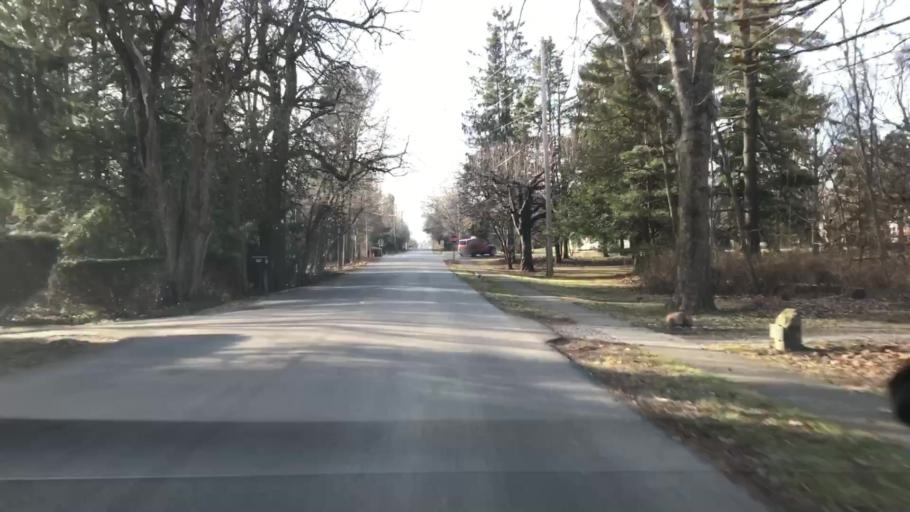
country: US
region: Ohio
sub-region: Greene County
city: Yellow Springs
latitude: 39.7935
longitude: -83.8894
